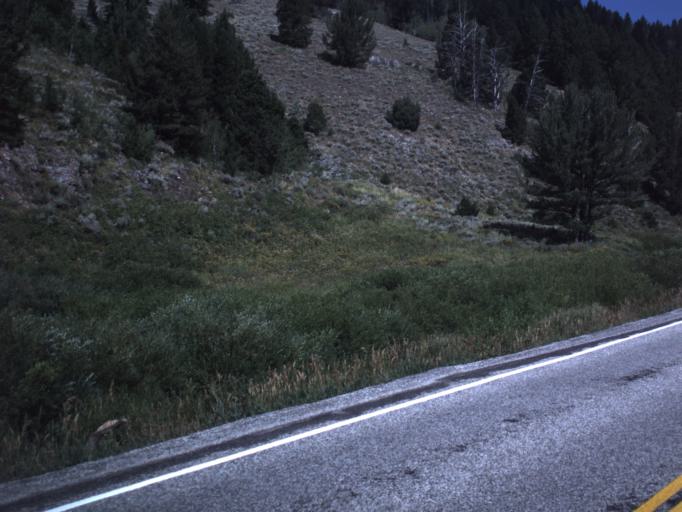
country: US
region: Utah
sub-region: Cache County
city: Richmond
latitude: 41.9557
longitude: -111.5418
